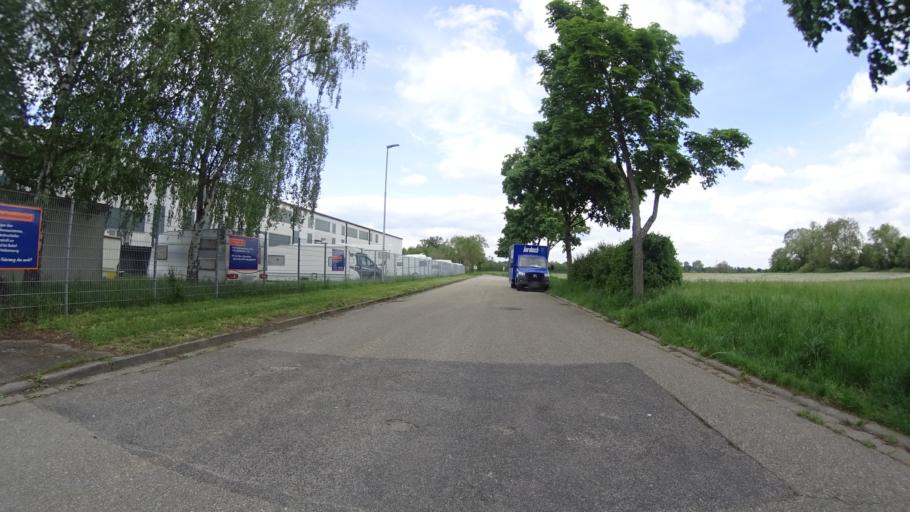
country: DE
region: Baden-Wuerttemberg
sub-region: Karlsruhe Region
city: Ettlingen
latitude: 48.9513
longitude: 8.3941
